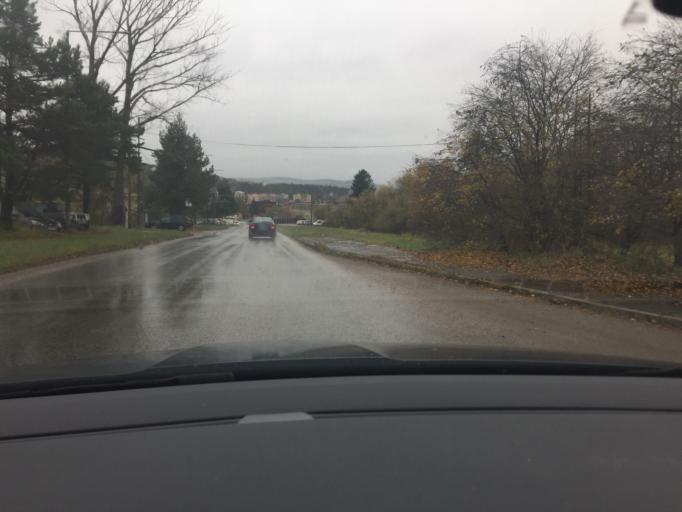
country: SK
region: Presovsky
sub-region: Okres Presov
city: Kezmarok
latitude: 49.1534
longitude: 20.4259
